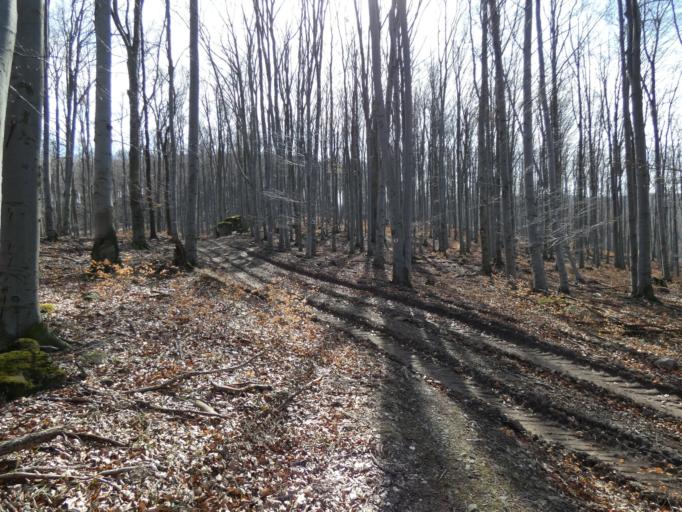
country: HU
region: Nograd
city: Diosjeno
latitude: 47.9764
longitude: 18.9551
